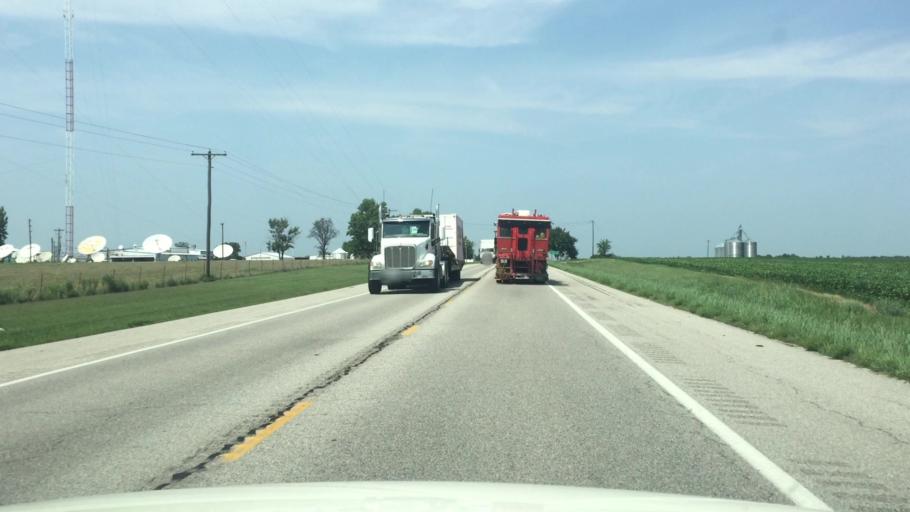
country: US
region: Missouri
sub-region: Jasper County
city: Carl Junction
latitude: 37.2185
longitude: -94.7048
